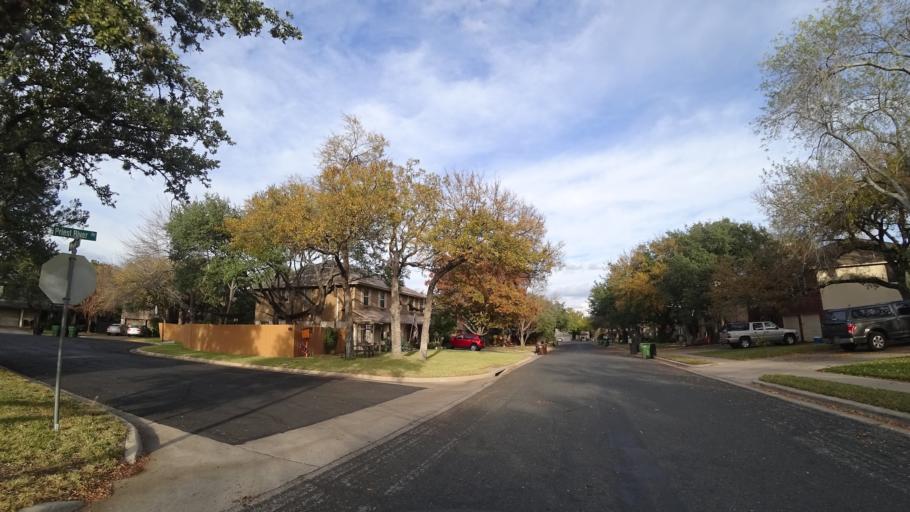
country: US
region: Texas
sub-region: Williamson County
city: Brushy Creek
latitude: 30.5118
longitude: -97.7272
